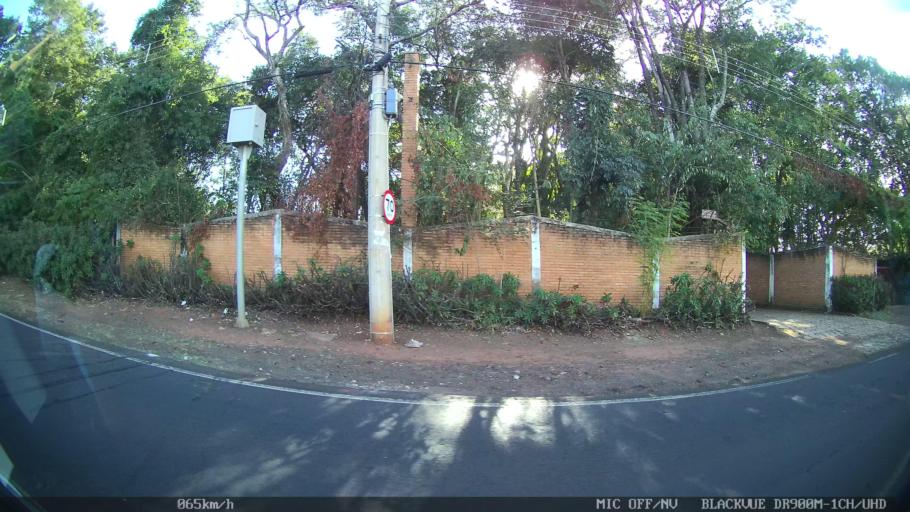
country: BR
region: Sao Paulo
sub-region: Araraquara
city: Araraquara
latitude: -21.7612
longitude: -48.1421
